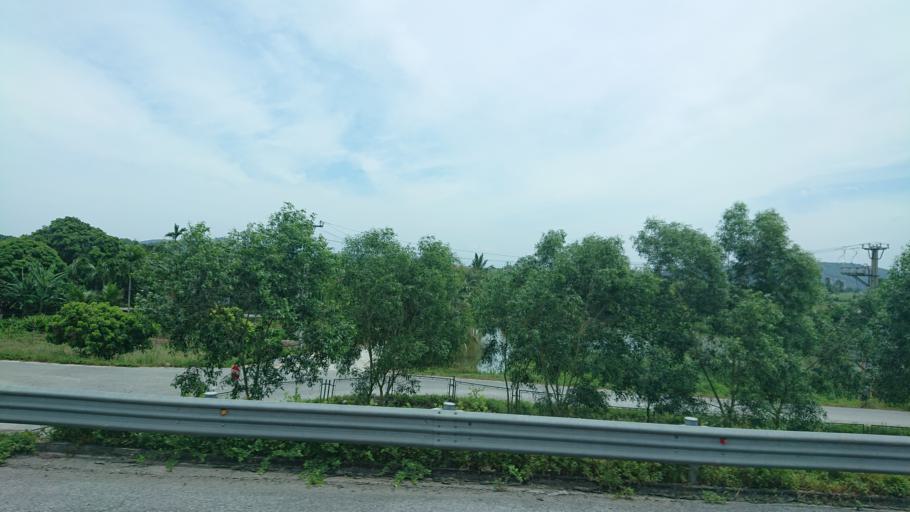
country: VN
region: Hai Phong
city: Tien Lang
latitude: 20.7720
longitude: 106.5847
